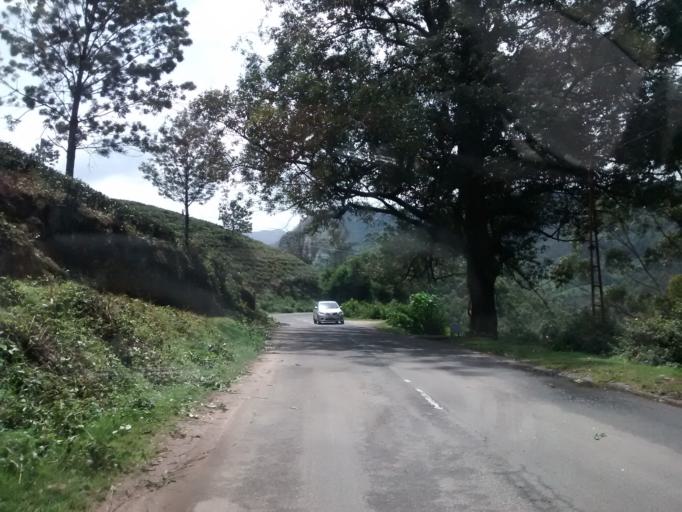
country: IN
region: Kerala
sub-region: Idukki
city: Munnar
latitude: 10.1028
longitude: 77.1128
